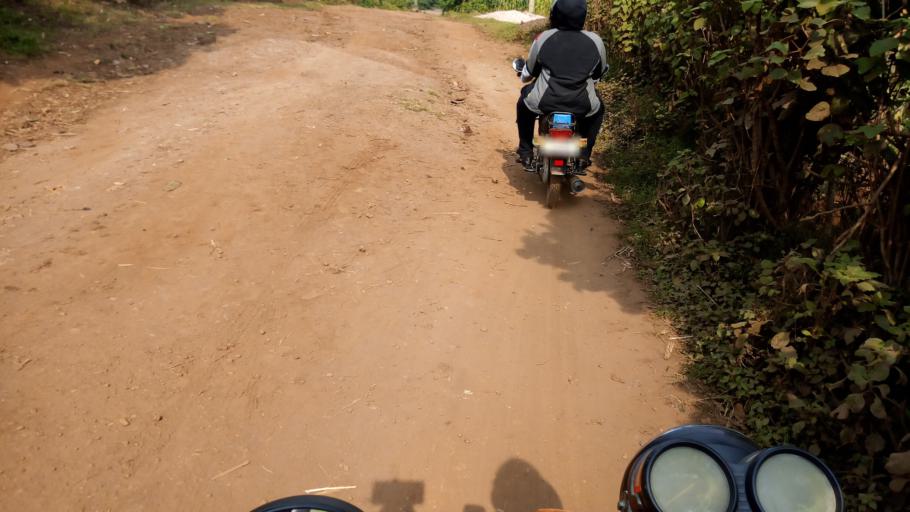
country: UG
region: Western Region
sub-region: Kisoro District
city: Kisoro
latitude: -1.3084
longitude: 29.6595
